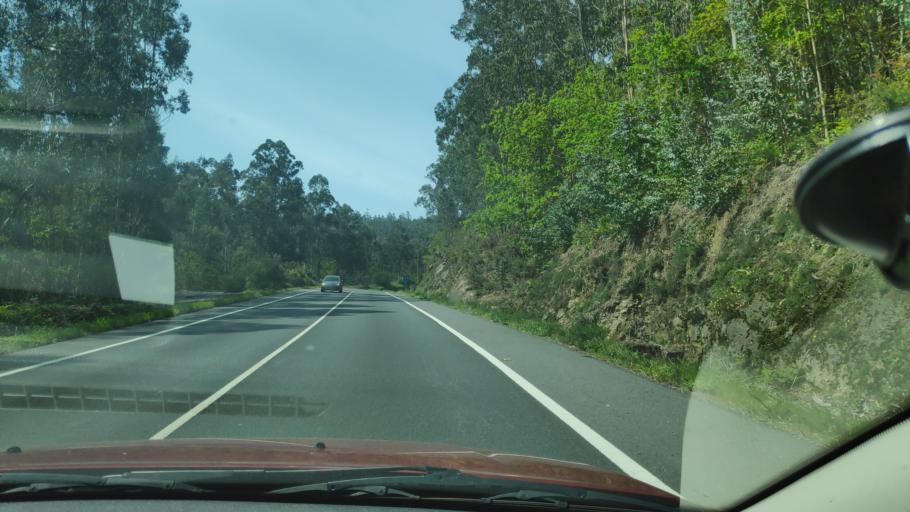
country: ES
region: Galicia
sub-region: Provincia da Coruna
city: Ames
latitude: 42.8754
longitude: -8.6601
